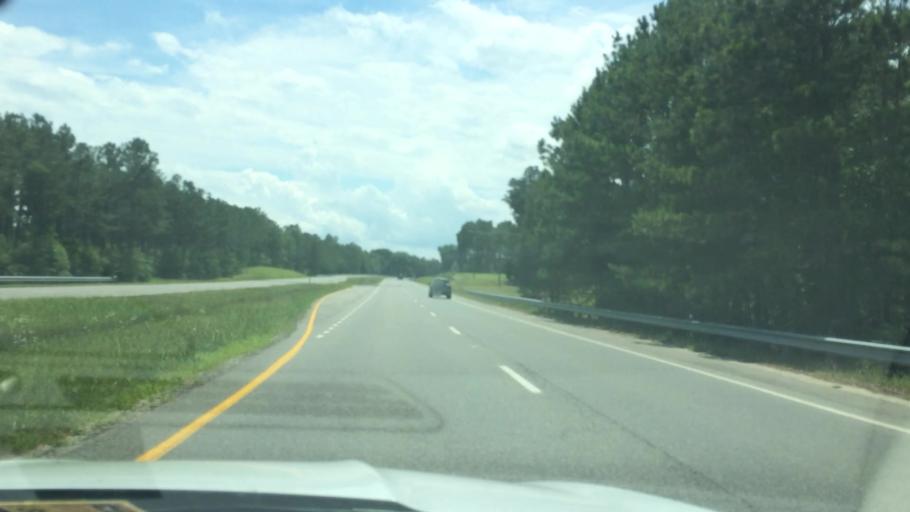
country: US
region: Virginia
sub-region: Middlesex County
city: Saluda
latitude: 37.5622
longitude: -76.6570
